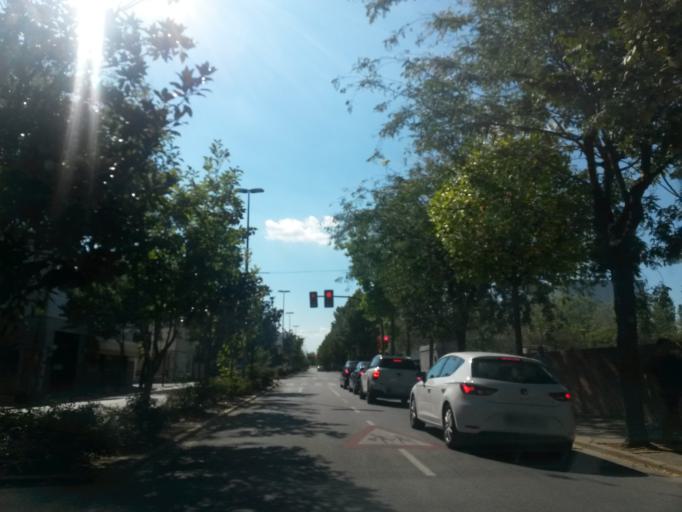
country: ES
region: Catalonia
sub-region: Provincia de Girona
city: Salt
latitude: 41.9707
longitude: 2.7866
